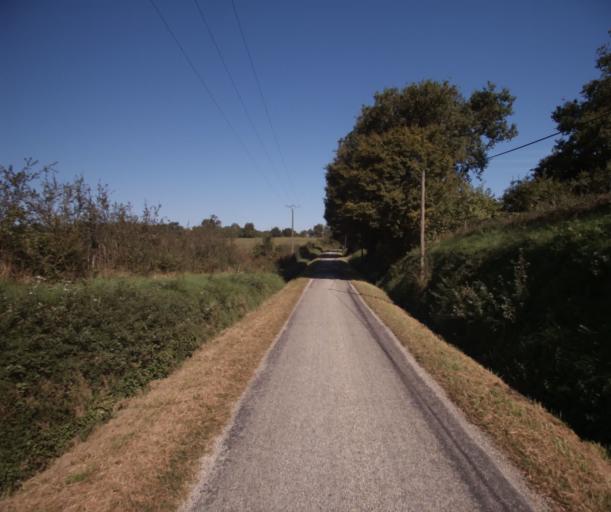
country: FR
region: Aquitaine
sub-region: Departement des Landes
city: Gabarret
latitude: 43.9450
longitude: -0.0131
